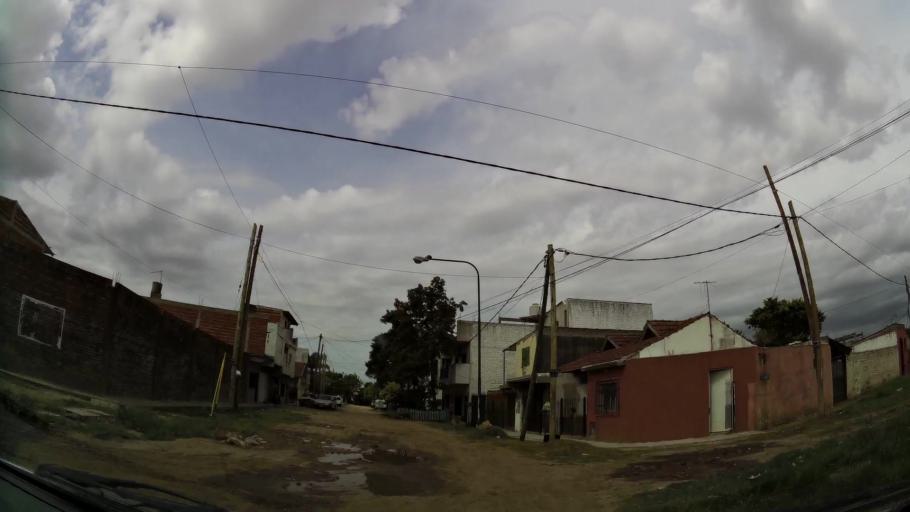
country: AR
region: Buenos Aires
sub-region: Partido de Quilmes
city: Quilmes
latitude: -34.7481
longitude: -58.2479
